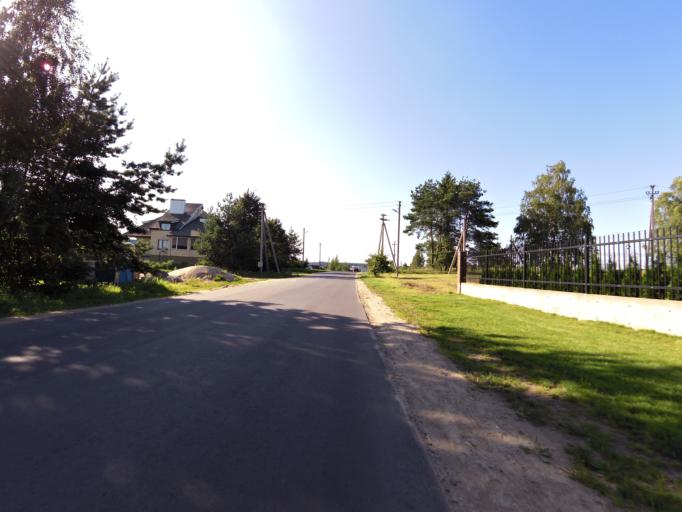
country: LT
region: Vilnius County
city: Pasilaiciai
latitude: 54.7300
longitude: 25.1908
